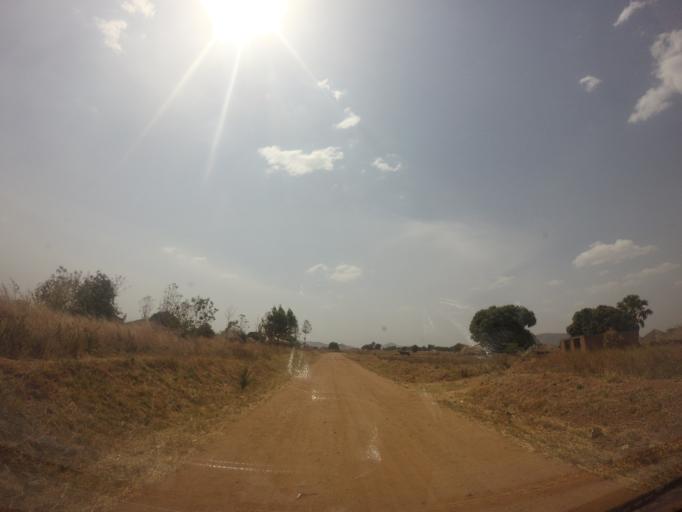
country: UG
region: Northern Region
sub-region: Arua District
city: Arua
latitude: 2.9085
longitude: 31.0568
